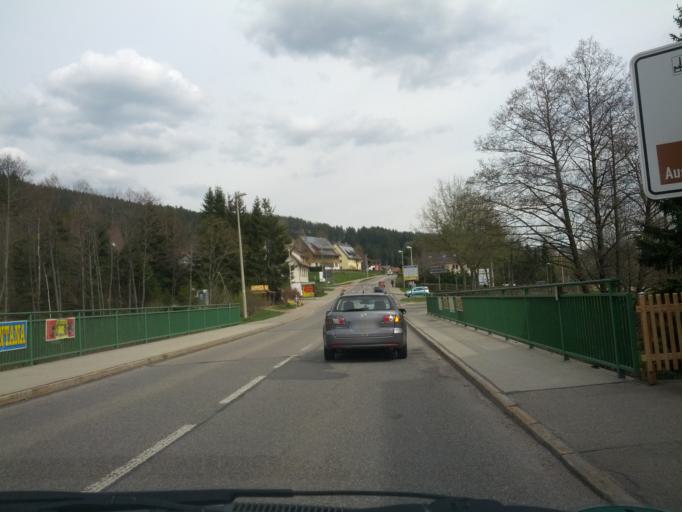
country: DE
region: Baden-Wuerttemberg
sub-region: Freiburg Region
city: Titisee-Neustadt
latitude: 47.9238
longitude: 8.1917
